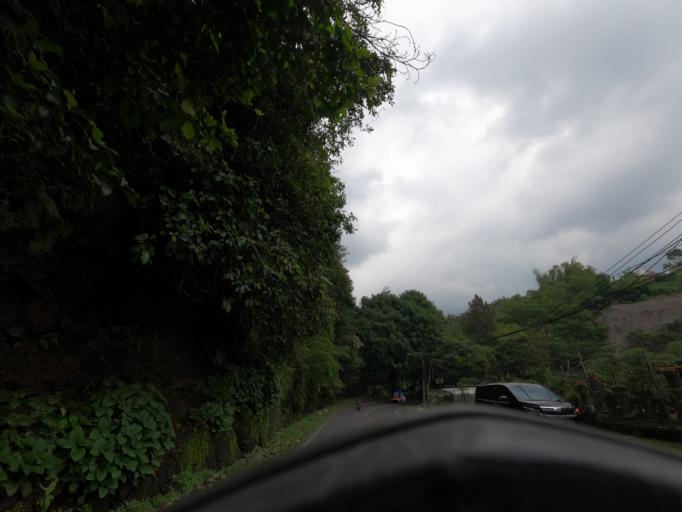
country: ID
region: West Java
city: Caringin
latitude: -6.7267
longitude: 107.0365
